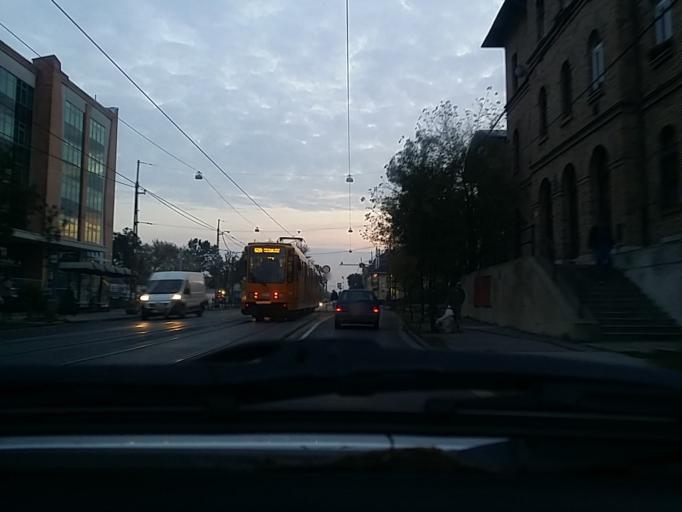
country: HU
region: Budapest
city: Budapest XIV. keruelet
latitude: 47.5354
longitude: 19.1133
